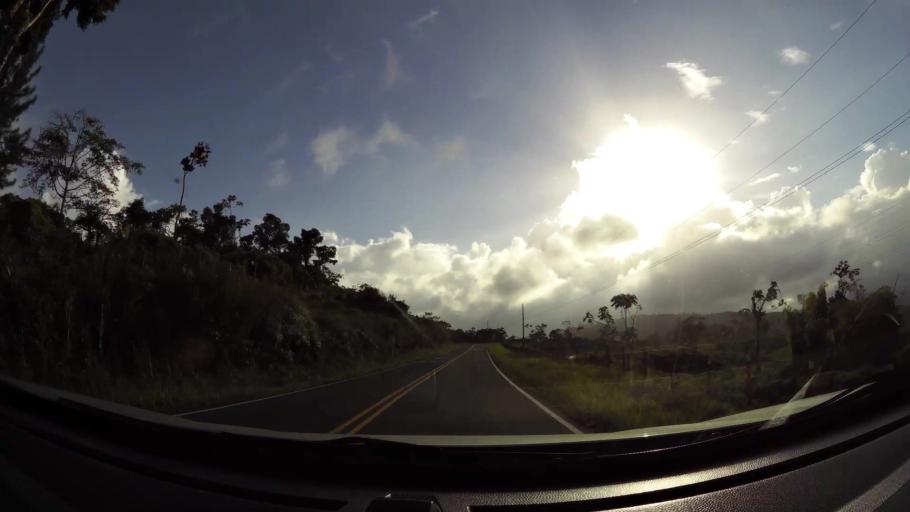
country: CR
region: Limon
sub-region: Canton de Siquirres
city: Siquirres
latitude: 10.0337
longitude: -83.5494
